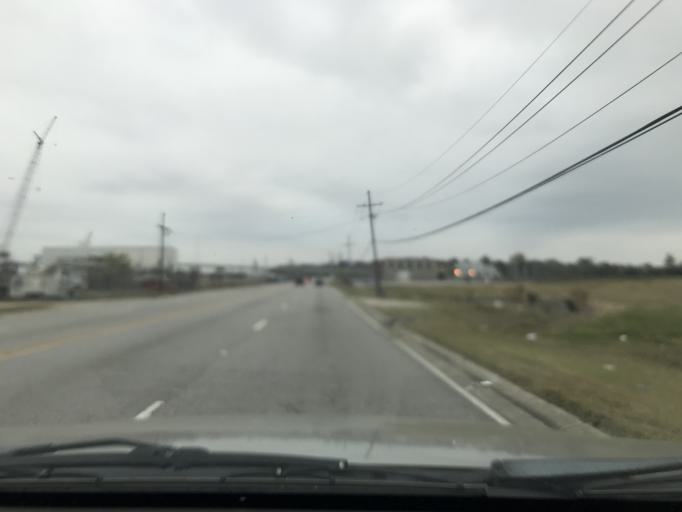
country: US
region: Louisiana
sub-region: Jefferson Parish
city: Woodmere
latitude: 29.8751
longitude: -90.0736
